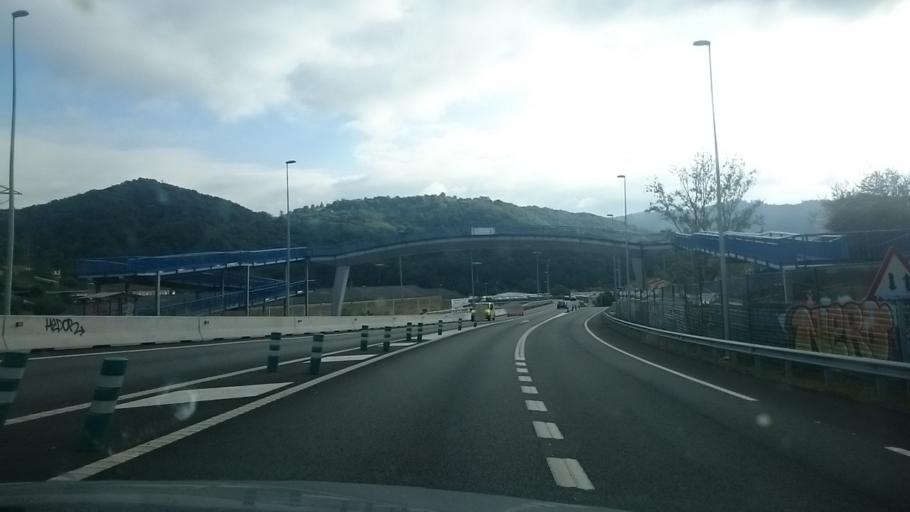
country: ES
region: Asturias
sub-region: Province of Asturias
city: Sama
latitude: 43.3267
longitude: -5.7152
